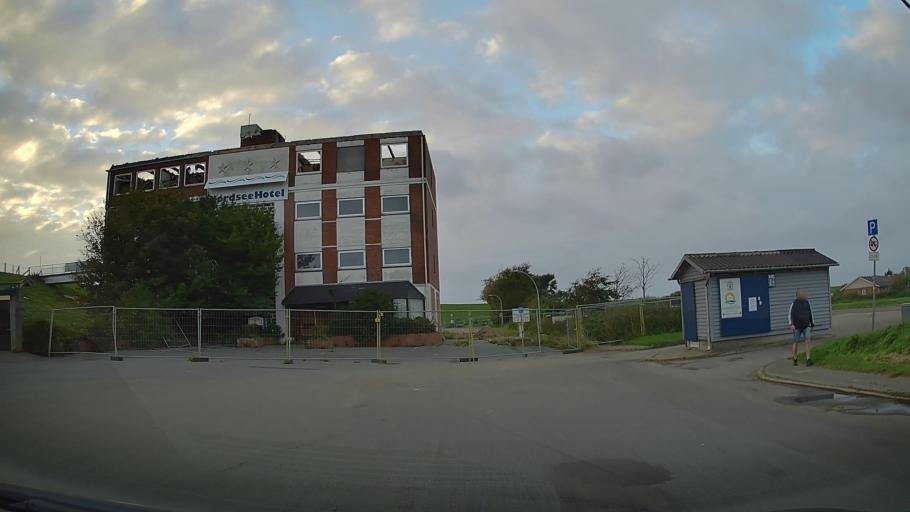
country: DE
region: Schleswig-Holstein
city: Schobull
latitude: 54.4778
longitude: 9.0105
